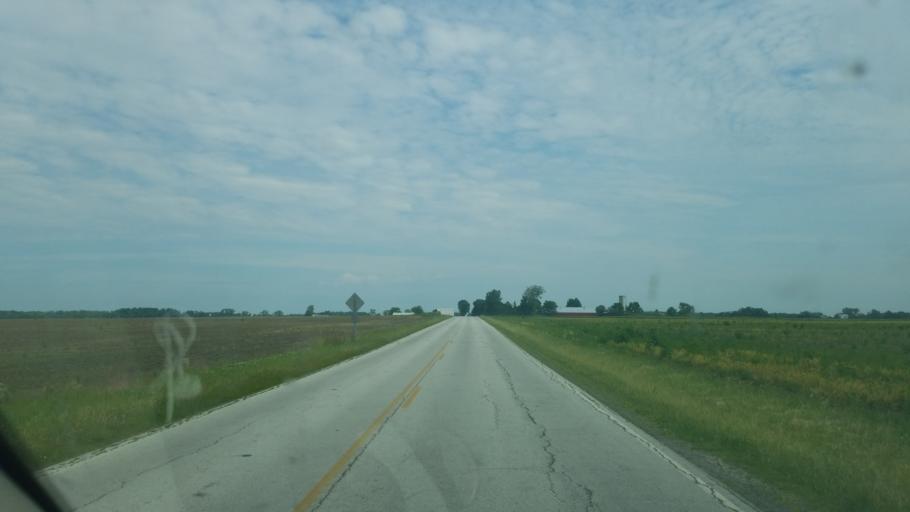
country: US
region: Ohio
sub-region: Seneca County
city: Fostoria
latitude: 41.0808
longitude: -83.4783
